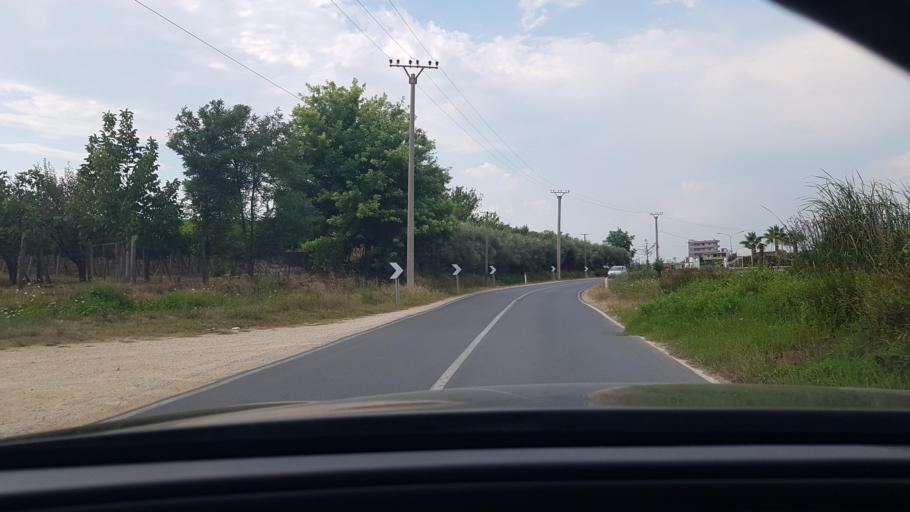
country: AL
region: Durres
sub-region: Rrethi i Durresit
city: Katundi i Ri
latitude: 41.4140
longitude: 19.5460
